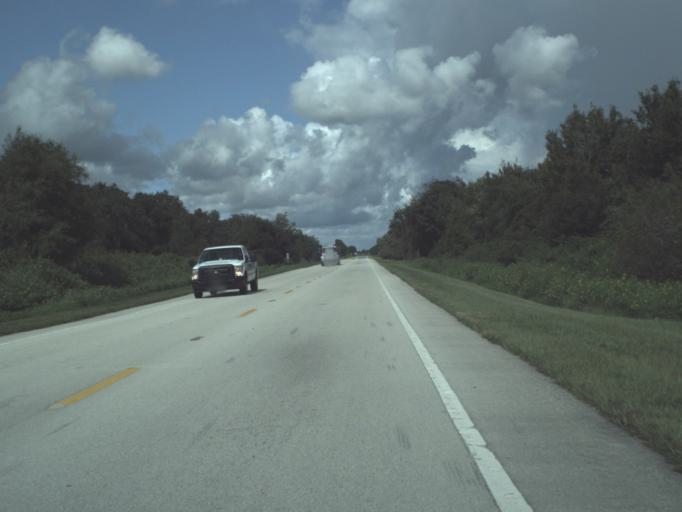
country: US
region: Florida
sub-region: DeSoto County
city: Arcadia
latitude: 27.2871
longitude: -82.0443
